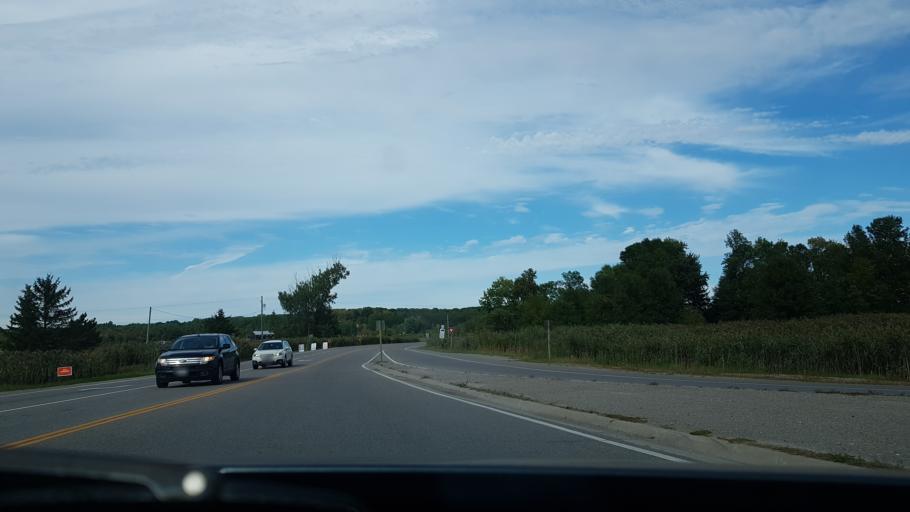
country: CA
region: Ontario
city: Angus
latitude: 44.4654
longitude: -79.8649
